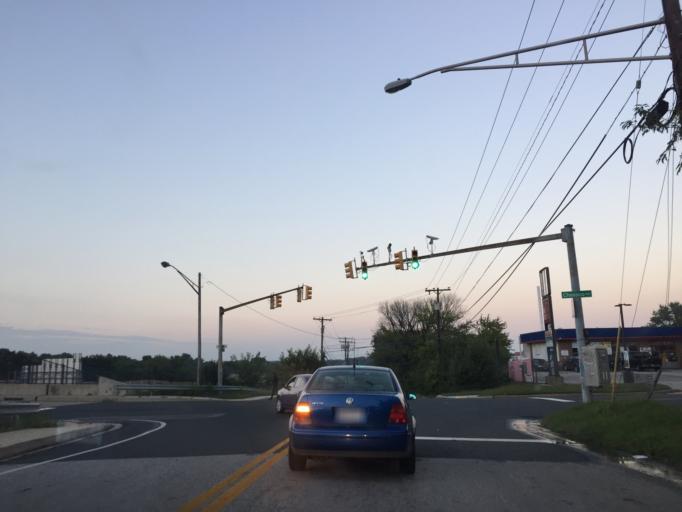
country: US
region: Maryland
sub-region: Baltimore County
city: Rosedale
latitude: 39.3297
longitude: -76.5218
